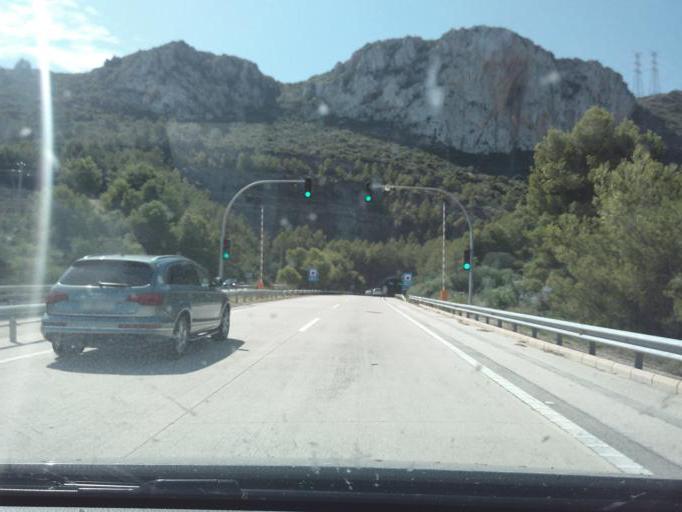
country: ES
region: Valencia
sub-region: Provincia de Valencia
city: Xeresa
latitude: 39.0052
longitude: -0.2249
